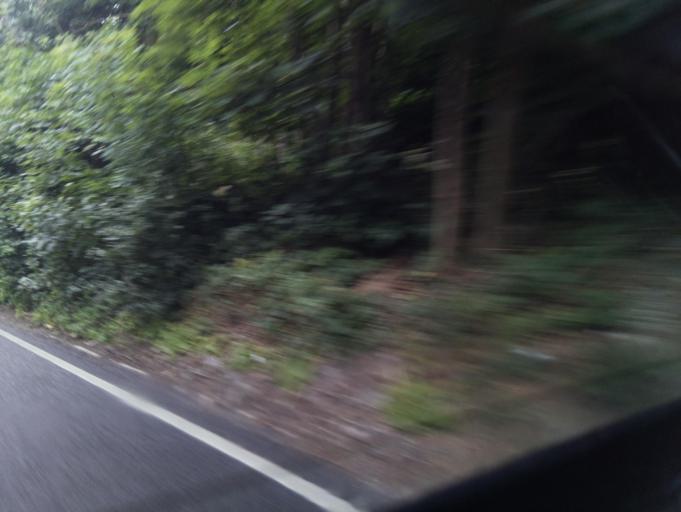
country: GB
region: England
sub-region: Surrey
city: Reigate
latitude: 51.2543
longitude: -0.1945
